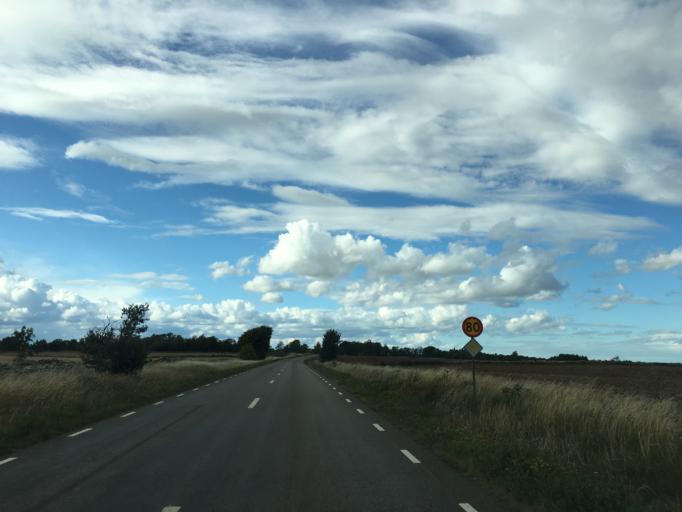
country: SE
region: Kalmar
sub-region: Morbylanga Kommun
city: Moerbylanga
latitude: 56.4083
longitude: 16.4359
